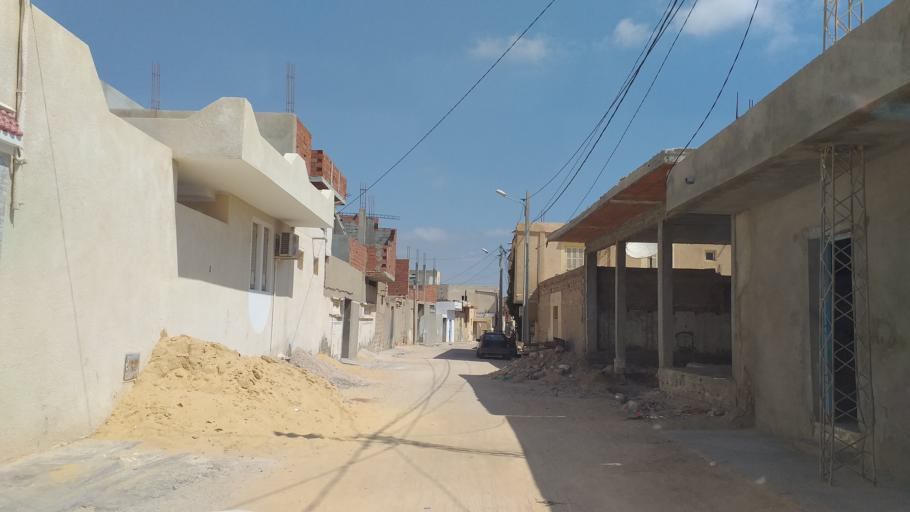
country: TN
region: Qabis
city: Gabes
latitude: 33.9425
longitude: 10.0662
